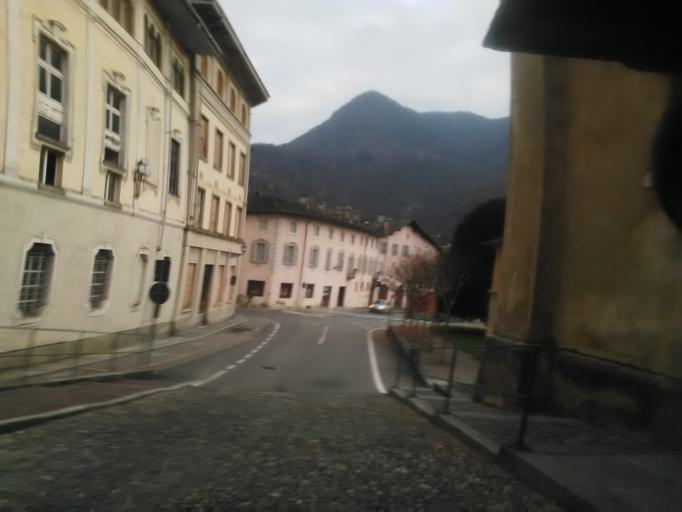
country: IT
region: Piedmont
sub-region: Provincia di Vercelli
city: Varallo
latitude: 45.8175
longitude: 8.2528
